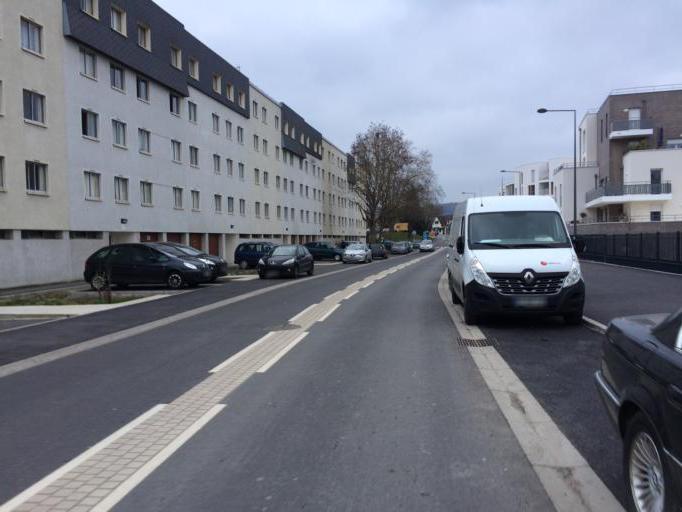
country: FR
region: Ile-de-France
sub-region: Departement de l'Essonne
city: Igny
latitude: 48.7319
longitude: 2.2311
